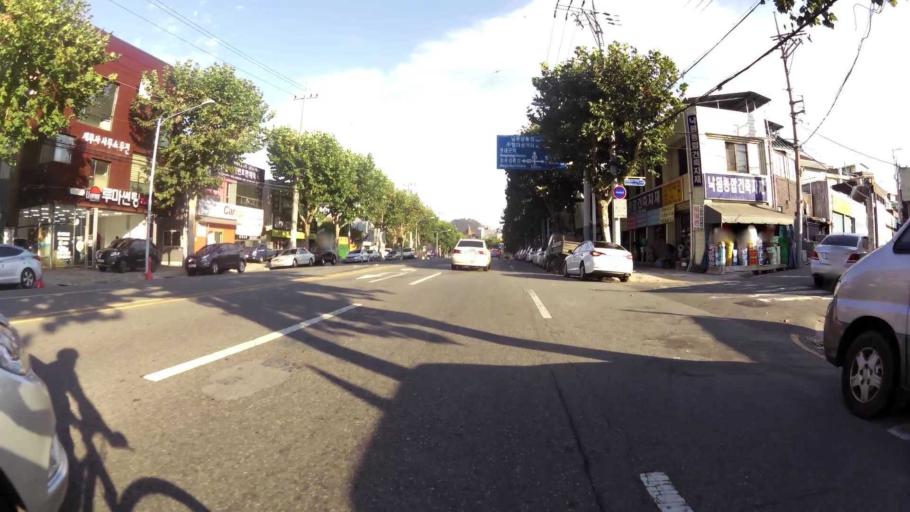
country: KR
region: Daegu
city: Daegu
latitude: 35.8669
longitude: 128.6366
